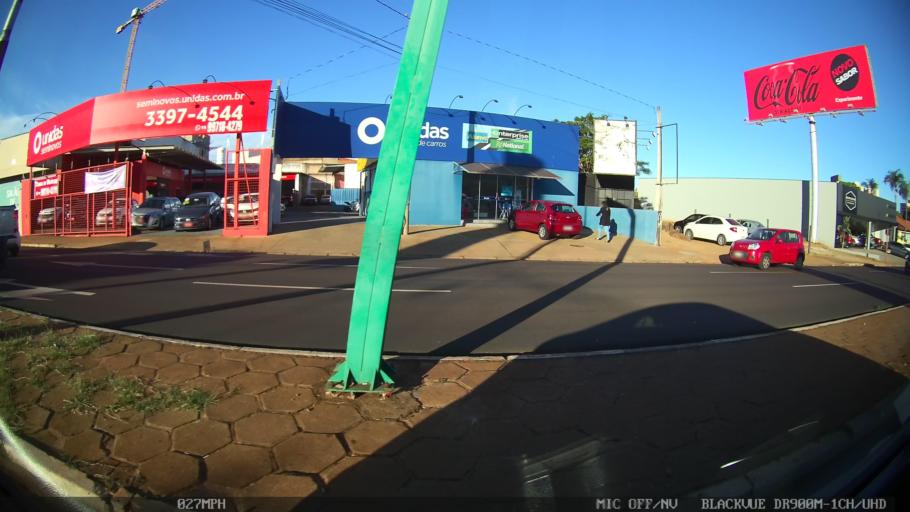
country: BR
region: Sao Paulo
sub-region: Araraquara
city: Araraquara
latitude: -21.8028
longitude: -48.1732
